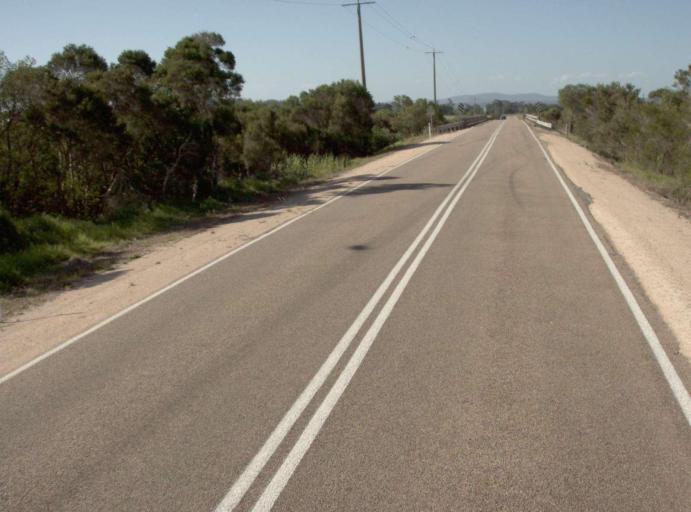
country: AU
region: Victoria
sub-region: East Gippsland
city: Lakes Entrance
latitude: -37.7800
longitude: 148.5393
